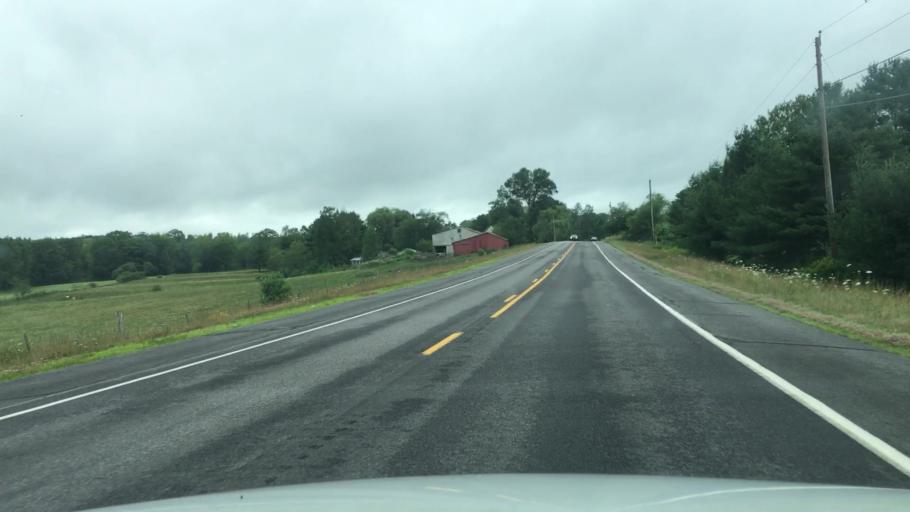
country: US
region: Maine
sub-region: Knox County
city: Union
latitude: 44.2161
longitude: -69.3081
